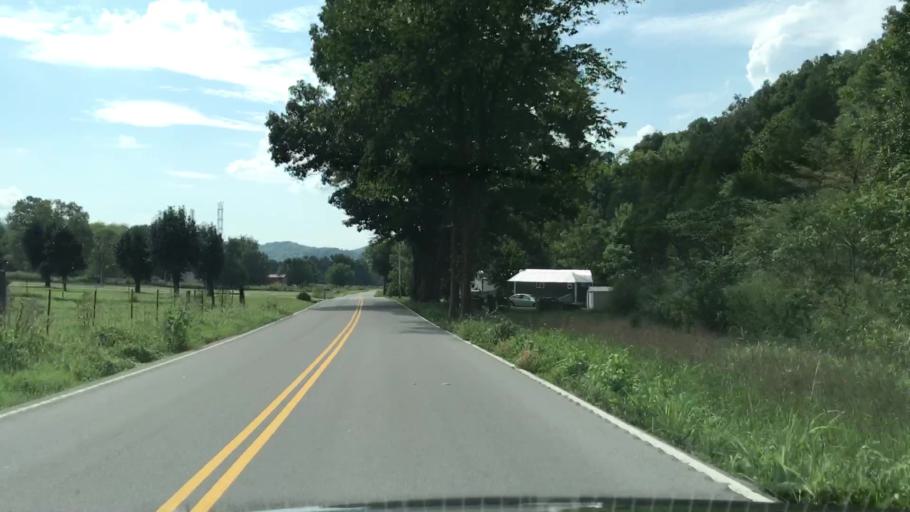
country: US
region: Tennessee
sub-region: Trousdale County
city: Hartsville
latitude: 36.4793
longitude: -86.1854
